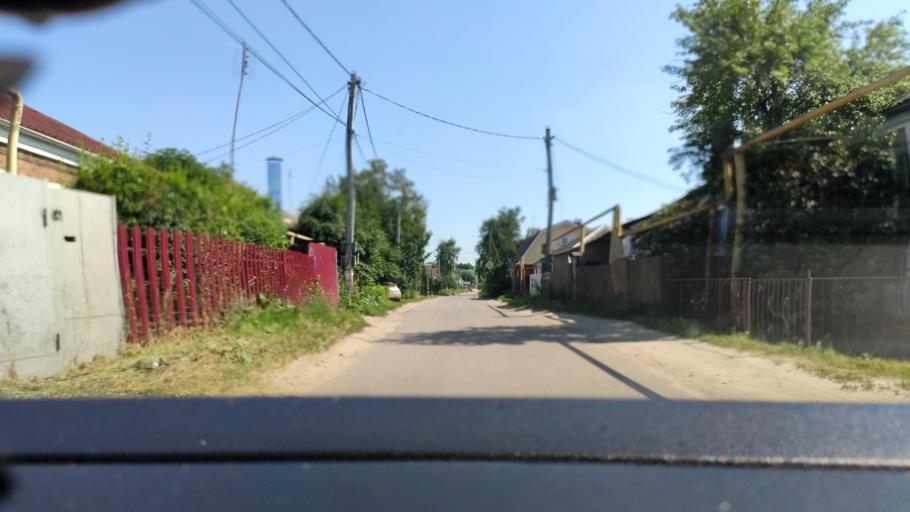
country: RU
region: Voronezj
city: Novaya Usman'
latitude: 51.6376
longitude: 39.4125
